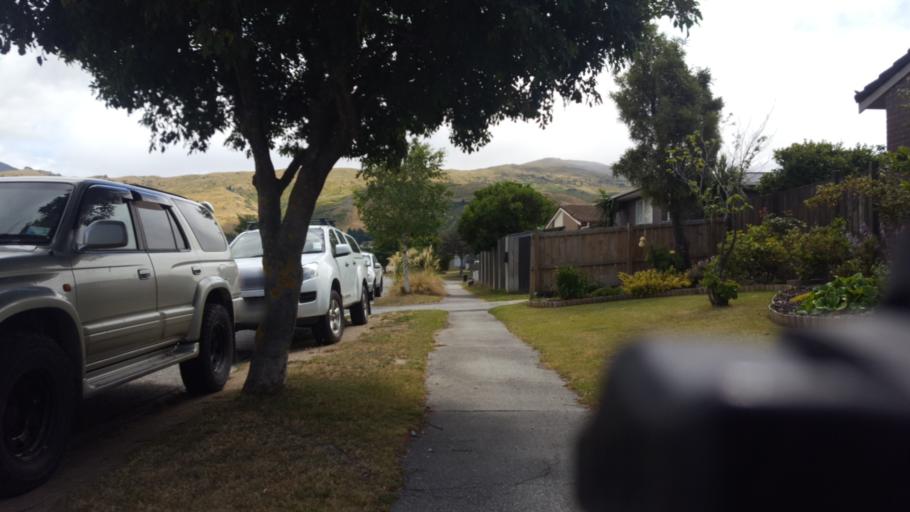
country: NZ
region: Otago
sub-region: Queenstown-Lakes District
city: Wanaka
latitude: -45.0416
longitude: 169.1828
